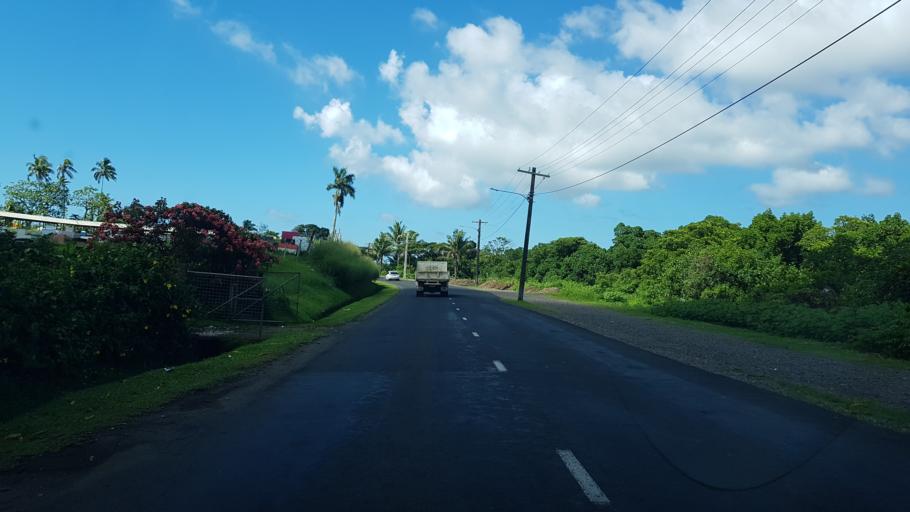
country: FJ
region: Central
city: Suva
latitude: -18.1403
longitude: 178.4568
